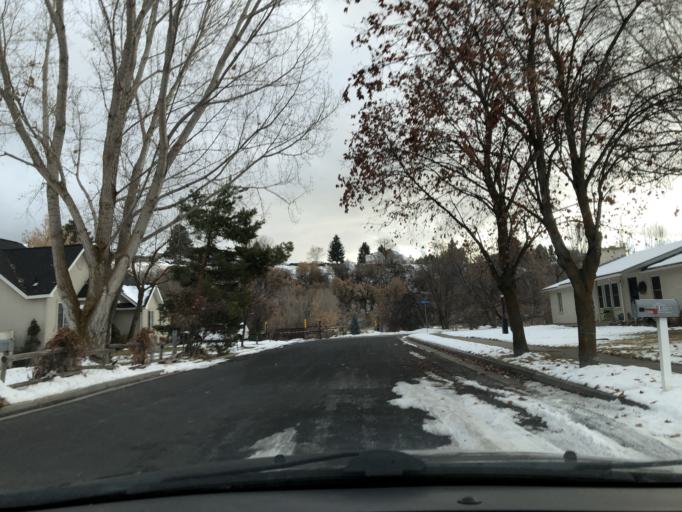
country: US
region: Utah
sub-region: Cache County
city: River Heights
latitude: 41.7298
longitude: -111.8175
